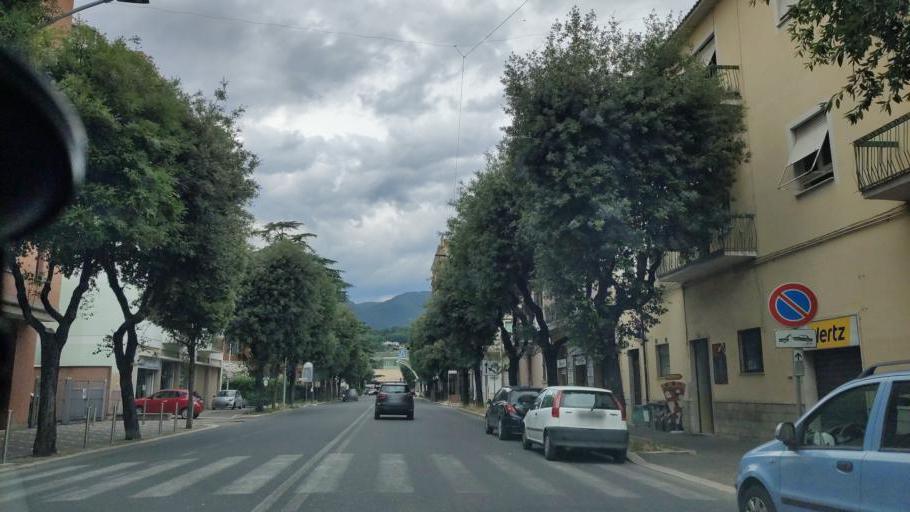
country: IT
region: Umbria
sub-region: Provincia di Terni
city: Terni
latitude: 42.5681
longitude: 12.6527
